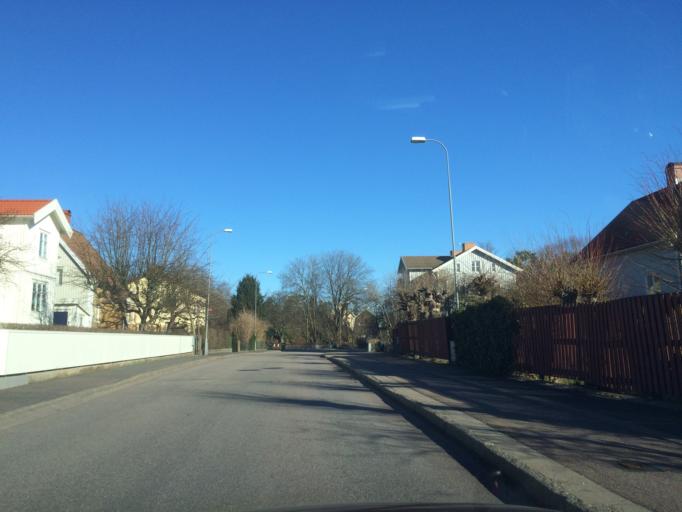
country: SE
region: Vaestra Goetaland
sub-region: Goteborg
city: Majorna
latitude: 57.6733
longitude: 11.8967
